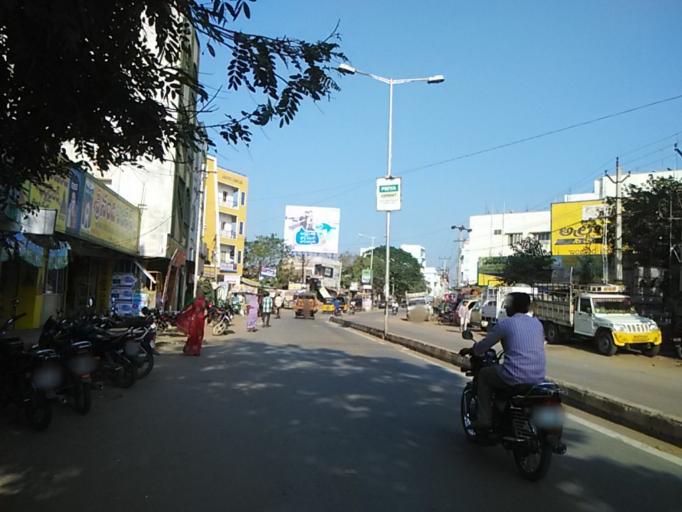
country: IN
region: Andhra Pradesh
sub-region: Kurnool
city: Nandyal
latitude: 15.4857
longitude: 78.4887
